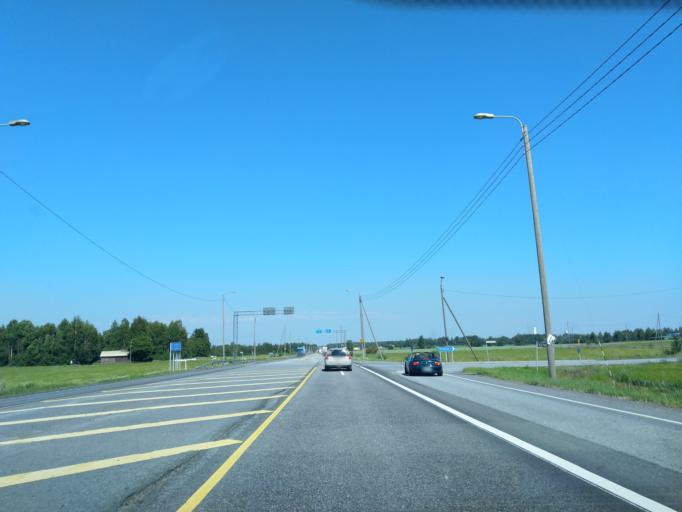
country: FI
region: Satakunta
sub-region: Pori
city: Nakkila
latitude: 61.3497
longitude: 22.0151
